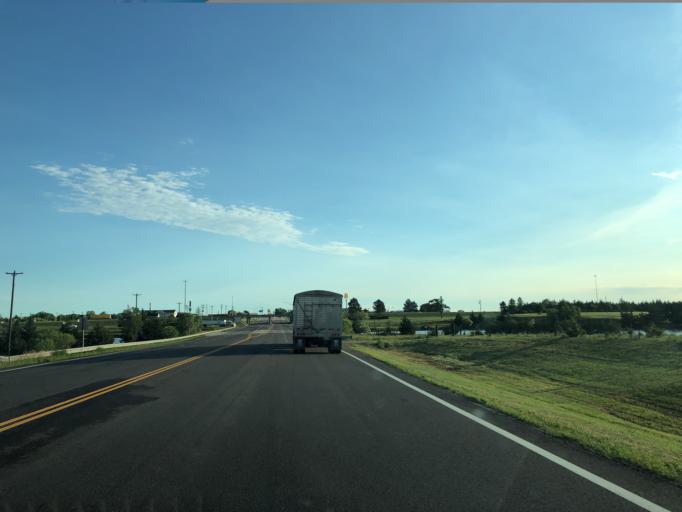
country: US
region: Kansas
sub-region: Russell County
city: Russell
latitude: 38.8603
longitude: -98.8545
